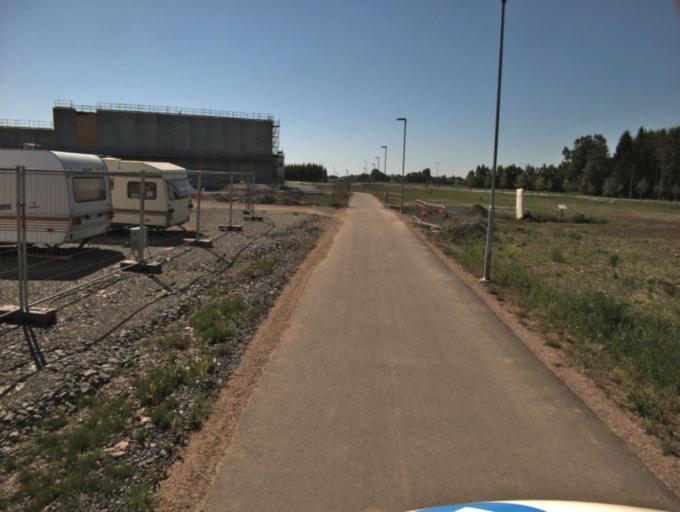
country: SE
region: Skane
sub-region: Kristianstads Kommun
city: Kristianstad
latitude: 56.0256
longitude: 14.1918
